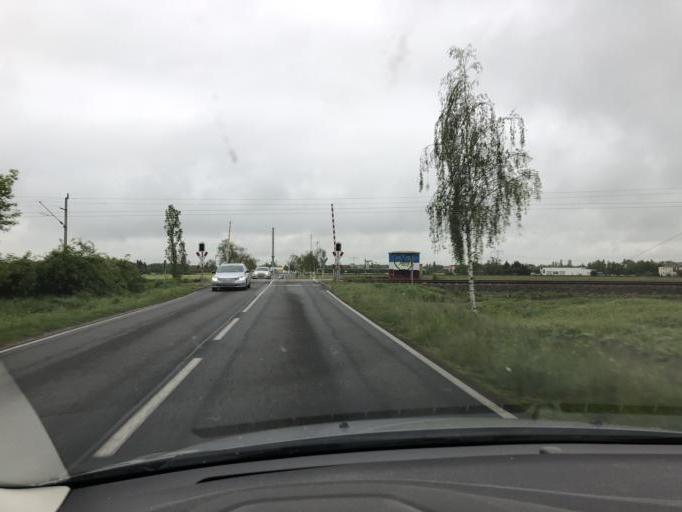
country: DE
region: Saxony
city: Dobernitz
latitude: 51.5202
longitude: 12.3658
